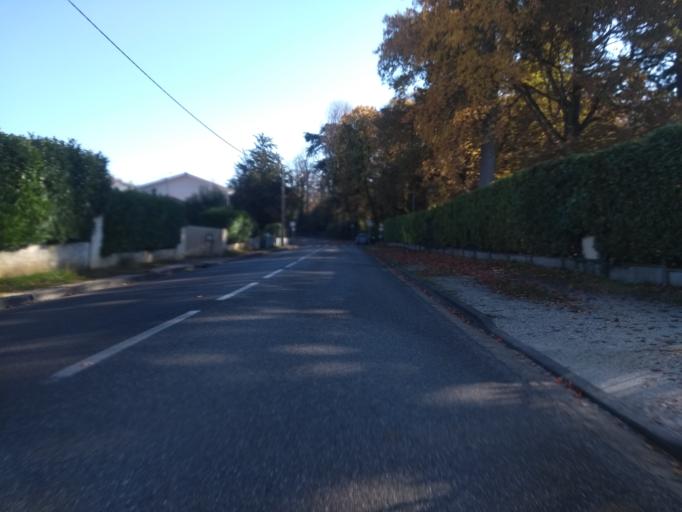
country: FR
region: Aquitaine
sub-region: Departement de la Gironde
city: Leognan
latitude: 44.7315
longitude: -0.5974
